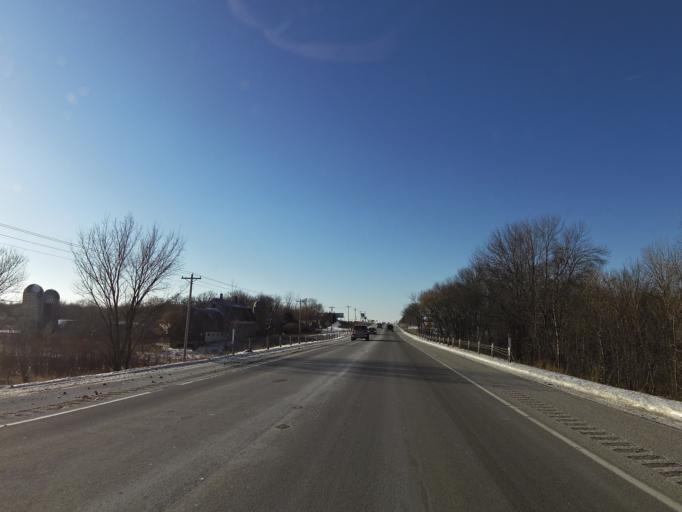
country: US
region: Minnesota
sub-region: Le Sueur County
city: New Prague
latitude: 44.5436
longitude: -93.5366
